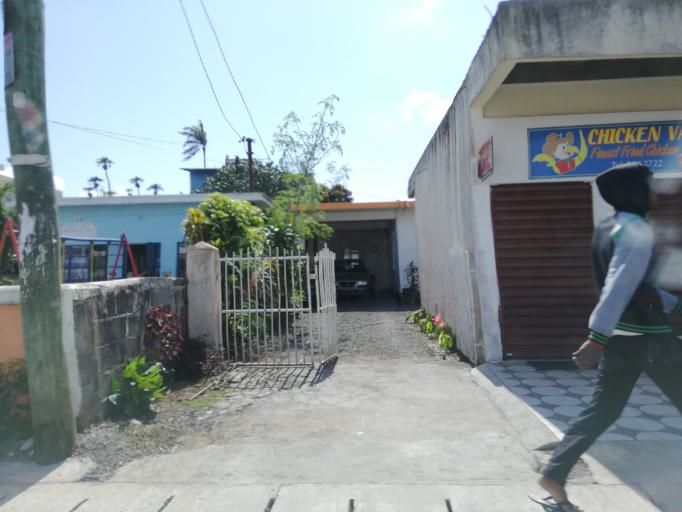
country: MU
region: Moka
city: Verdun
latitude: -20.2206
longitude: 57.5349
